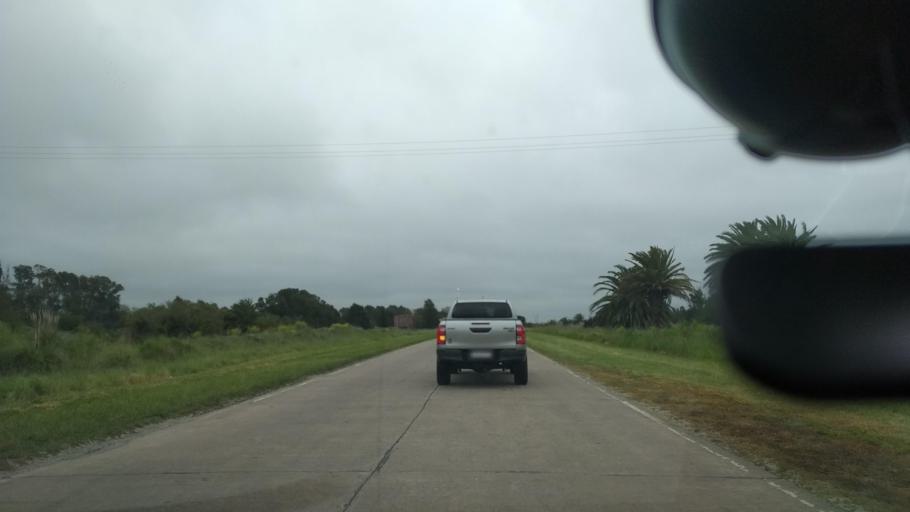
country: AR
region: Buenos Aires
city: Veronica
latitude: -35.5360
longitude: -57.3197
